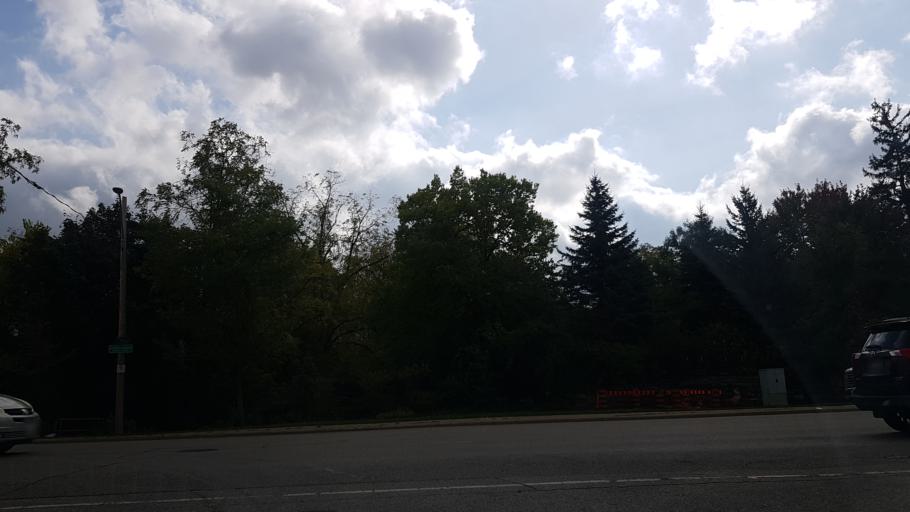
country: CA
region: Ontario
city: London
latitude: 42.9577
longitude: -81.2456
